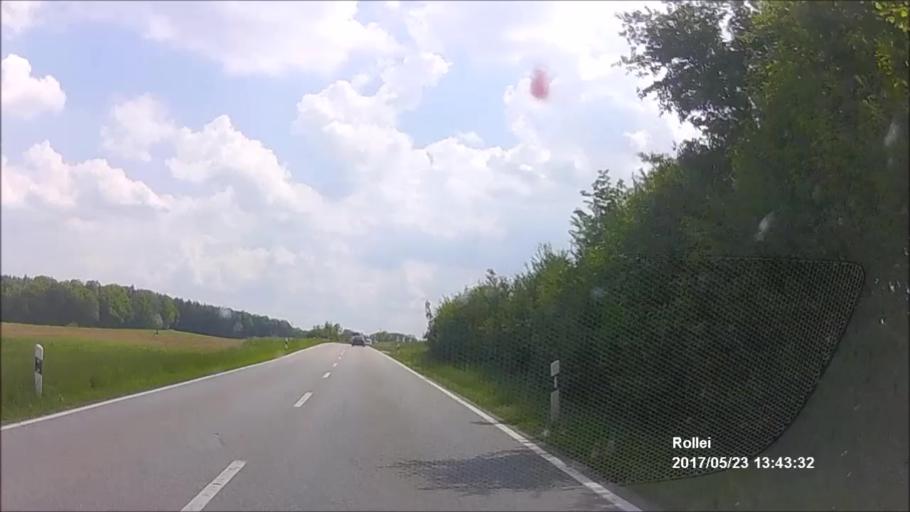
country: DE
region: Bavaria
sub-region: Upper Bavaria
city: Sankt Wolfgang
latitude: 48.1986
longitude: 12.1457
